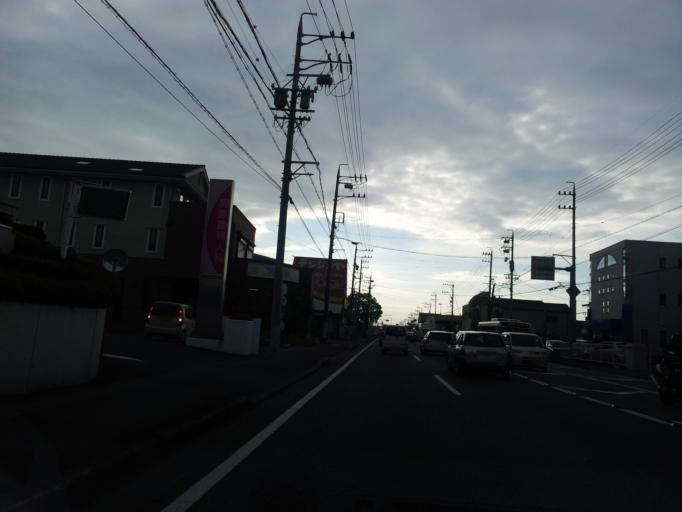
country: JP
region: Shizuoka
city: Shizuoka-shi
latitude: 34.9923
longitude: 138.4952
